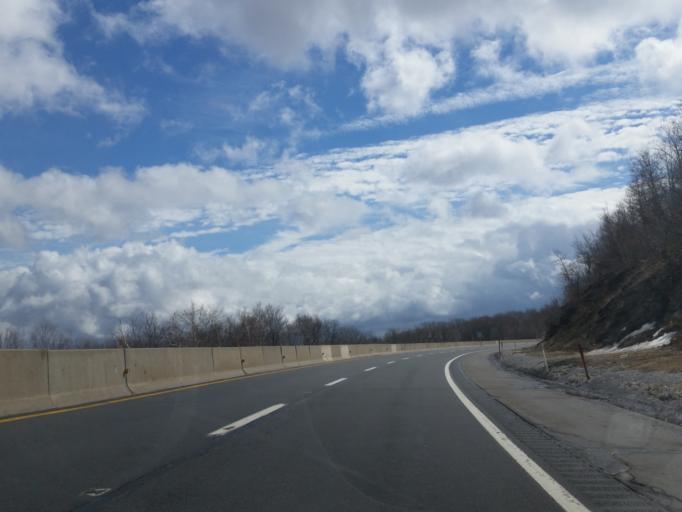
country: US
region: Pennsylvania
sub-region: Lackawanna County
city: Chinchilla
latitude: 41.4585
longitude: -75.6862
